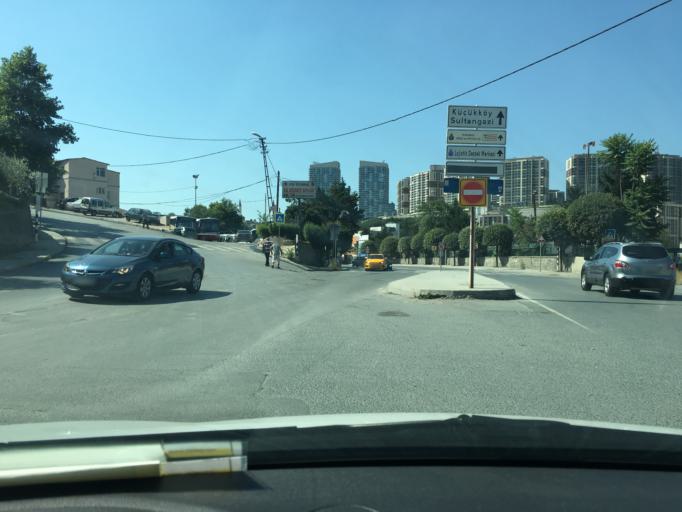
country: TR
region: Istanbul
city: Sisli
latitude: 41.0836
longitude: 28.9484
